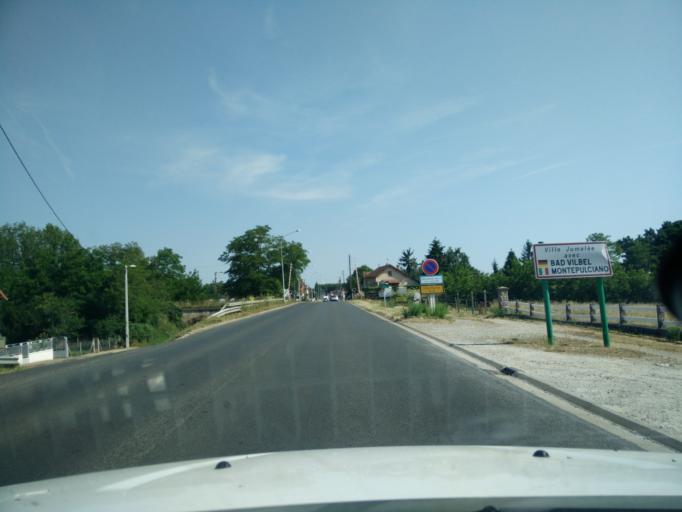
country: FR
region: Auvergne
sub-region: Departement de l'Allier
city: Moulins
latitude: 46.5531
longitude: 3.3209
